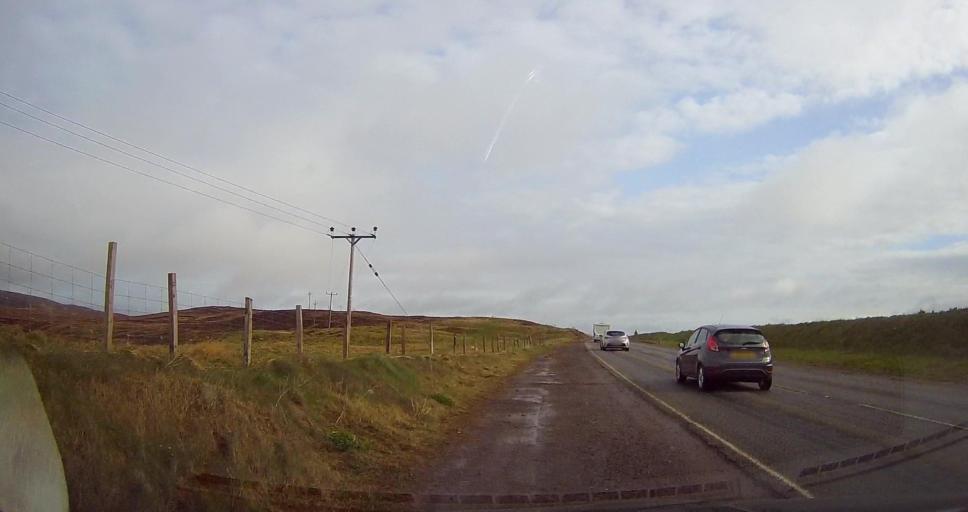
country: GB
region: Scotland
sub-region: Shetland Islands
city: Lerwick
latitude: 60.1149
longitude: -1.2183
